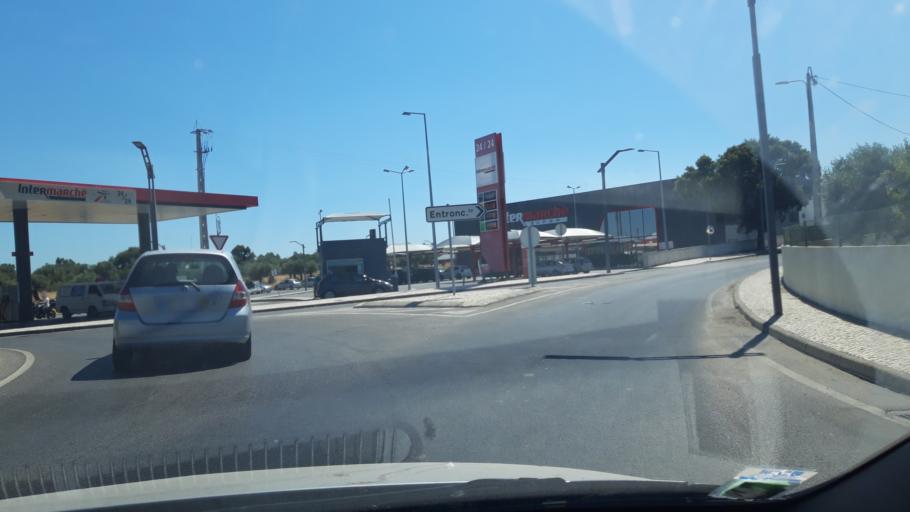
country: PT
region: Santarem
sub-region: Entroncamento
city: Entroncamento
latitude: 39.4621
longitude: -8.4519
